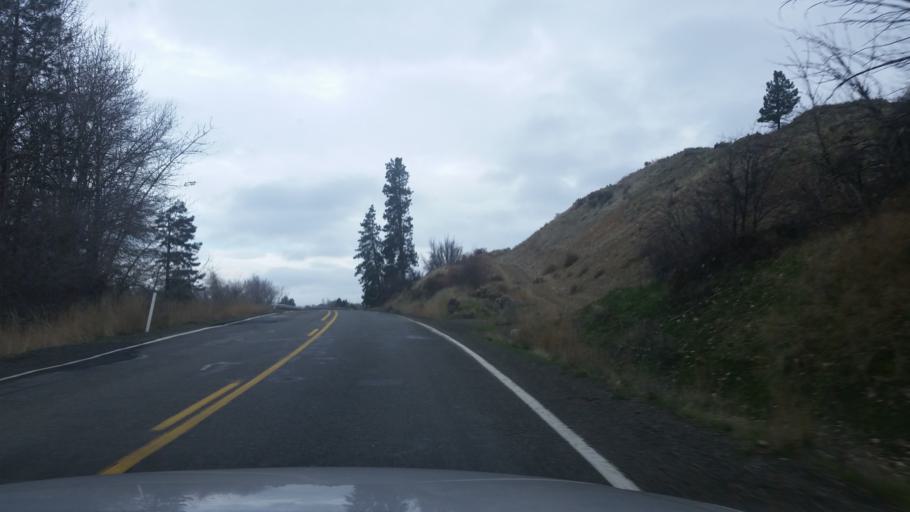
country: US
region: Washington
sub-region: Kittitas County
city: Ellensburg
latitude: 47.0697
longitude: -120.6558
